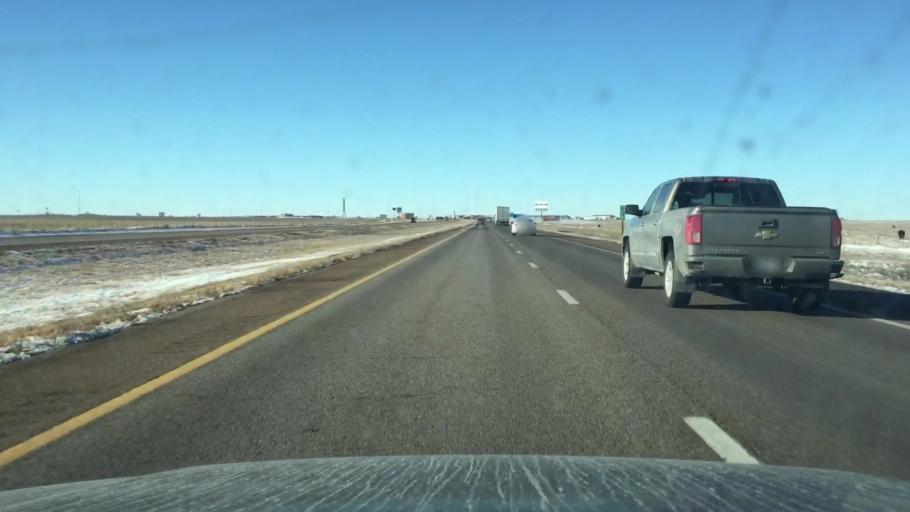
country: US
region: Kansas
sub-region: Thomas County
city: Colby
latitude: 39.3534
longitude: -101.0224
